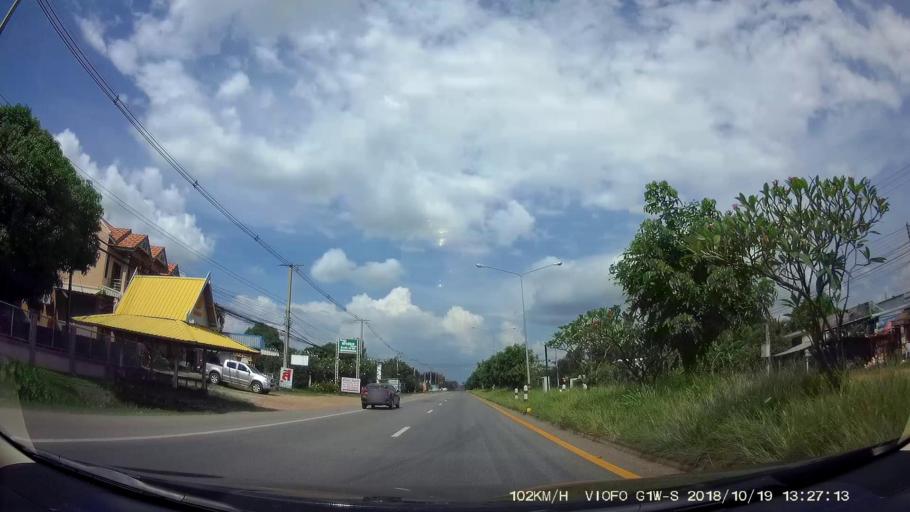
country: TH
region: Chaiyaphum
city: Chatturat
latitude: 15.5451
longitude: 101.8392
